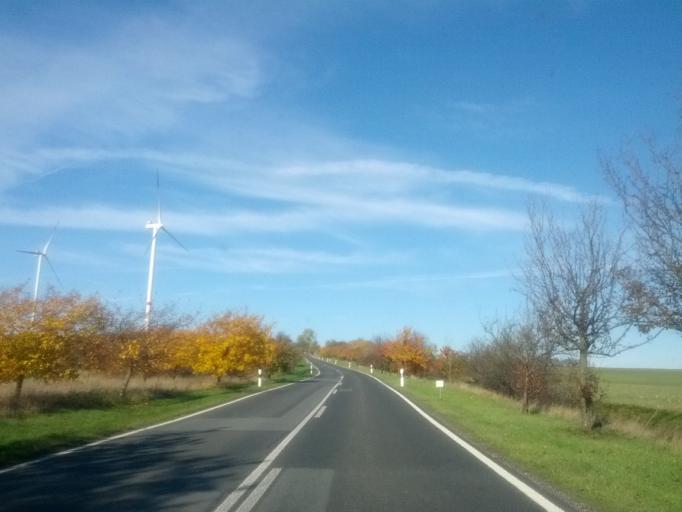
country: DE
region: Thuringia
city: Mechterstadt
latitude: 50.9515
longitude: 10.5585
